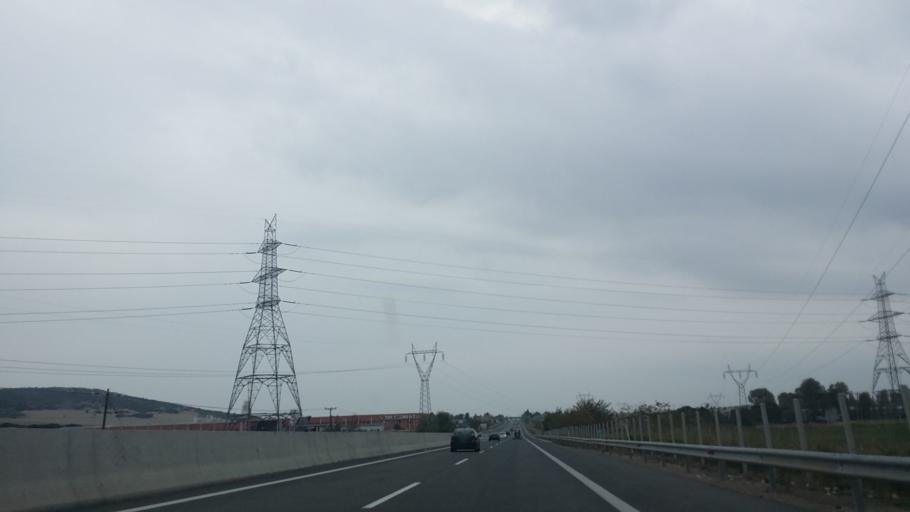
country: GR
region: Central Greece
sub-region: Nomos Voiotias
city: Arma
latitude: 38.3779
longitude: 23.4683
